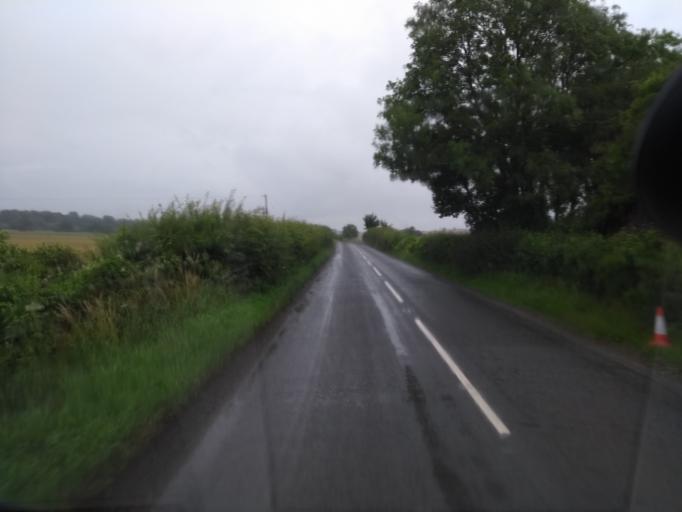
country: GB
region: England
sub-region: Somerset
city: Ilchester
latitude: 51.0597
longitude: -2.7007
